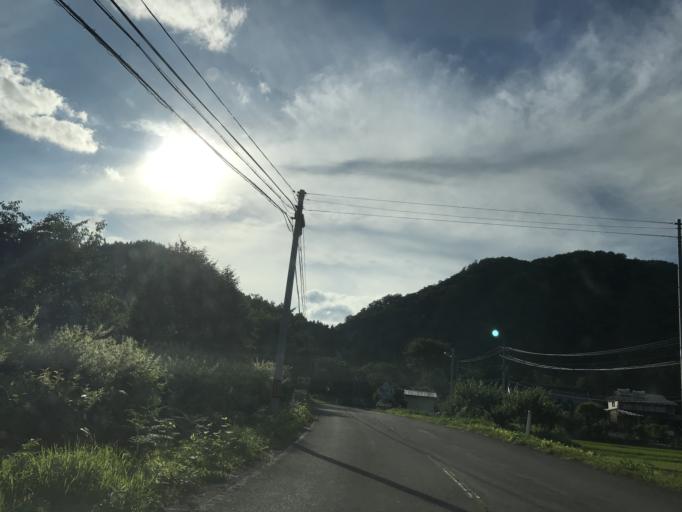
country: JP
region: Iwate
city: Ichinoseki
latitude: 38.9012
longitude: 140.9318
